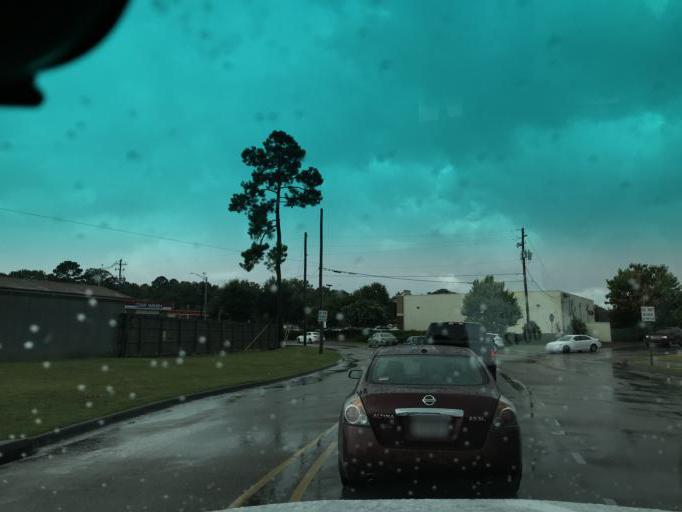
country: US
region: Alabama
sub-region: Montgomery County
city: Montgomery
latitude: 32.3676
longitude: -86.2700
